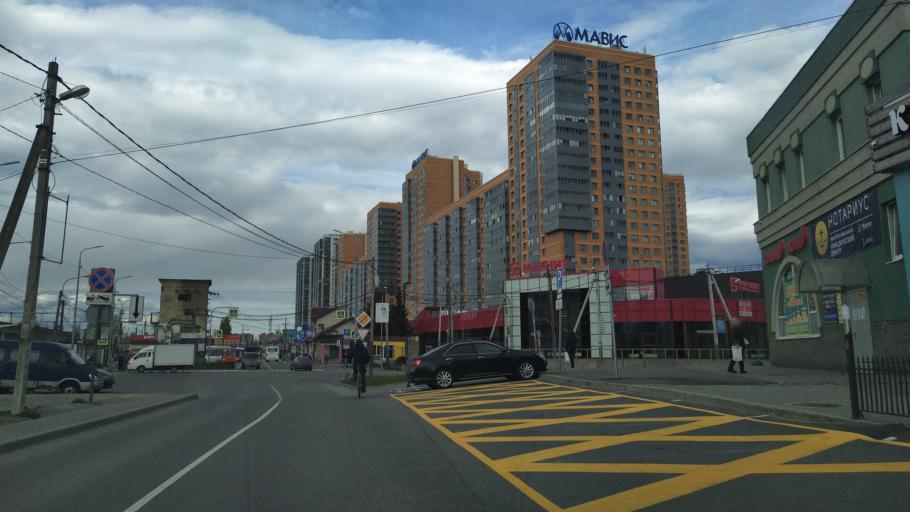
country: RU
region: Leningrad
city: Murino
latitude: 60.0487
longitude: 30.4427
